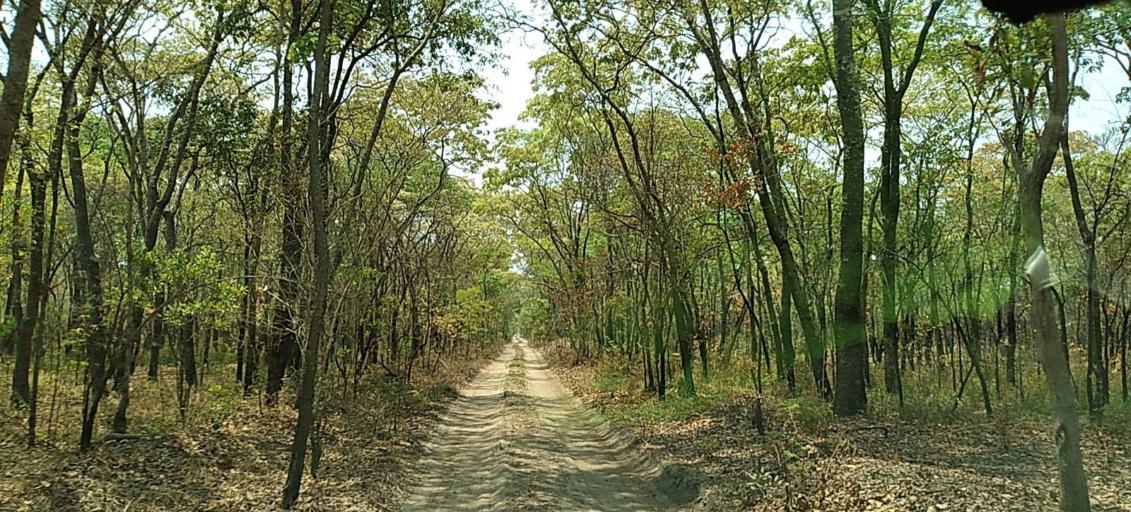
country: ZM
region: North-Western
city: Kabompo
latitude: -13.6560
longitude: 24.4649
